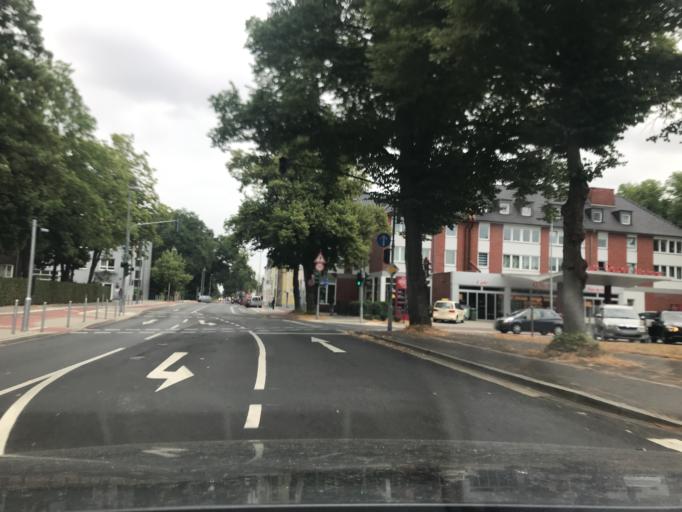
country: DE
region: North Rhine-Westphalia
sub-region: Regierungsbezirk Dusseldorf
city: Erkrath
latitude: 51.1799
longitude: 6.8748
